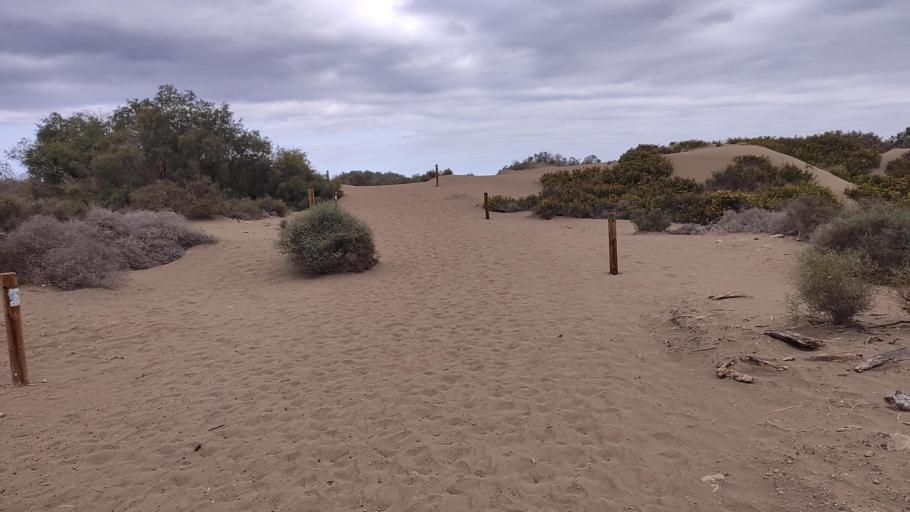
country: ES
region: Canary Islands
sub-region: Provincia de Las Palmas
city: Playa del Ingles
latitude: 27.7451
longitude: -15.5808
